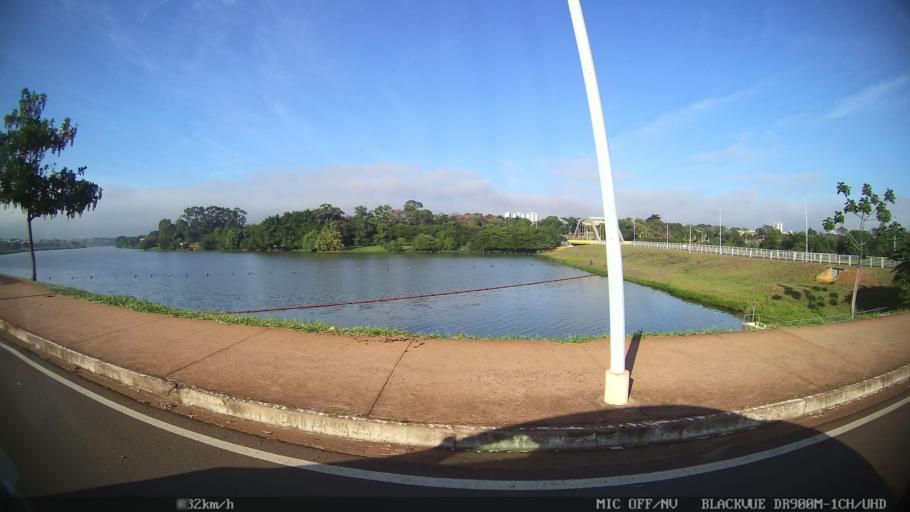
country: BR
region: Sao Paulo
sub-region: Sao Jose Do Rio Preto
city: Sao Jose do Rio Preto
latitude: -20.8101
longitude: -49.3529
